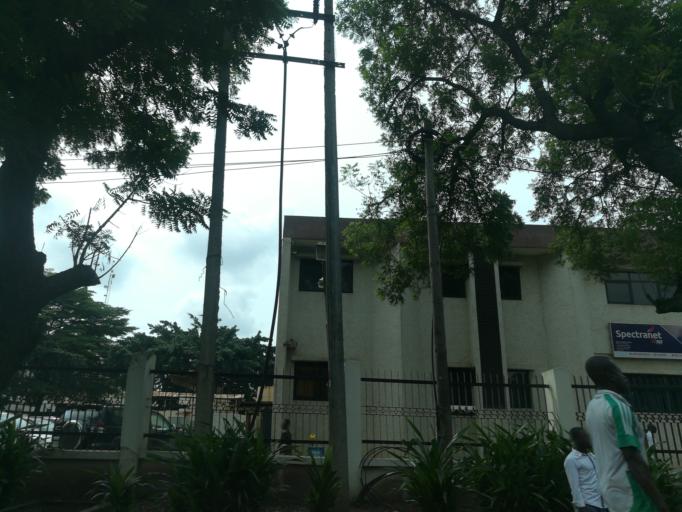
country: NG
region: Lagos
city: Ojota
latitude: 6.6001
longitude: 3.3761
